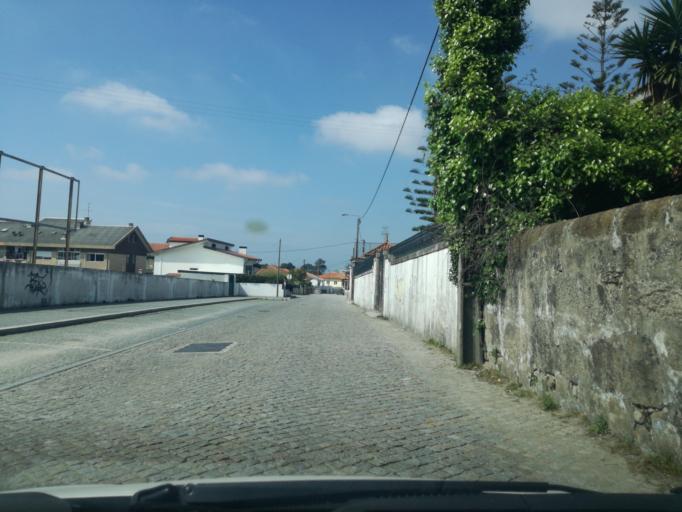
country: PT
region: Porto
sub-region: Maia
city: Gemunde
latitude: 41.2483
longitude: -8.6642
